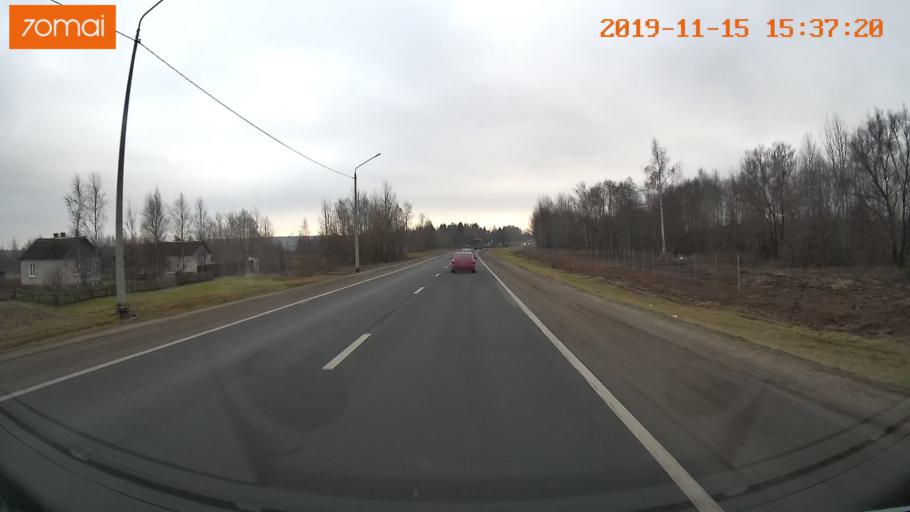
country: RU
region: Jaroslavl
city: Danilov
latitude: 58.0407
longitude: 40.0881
